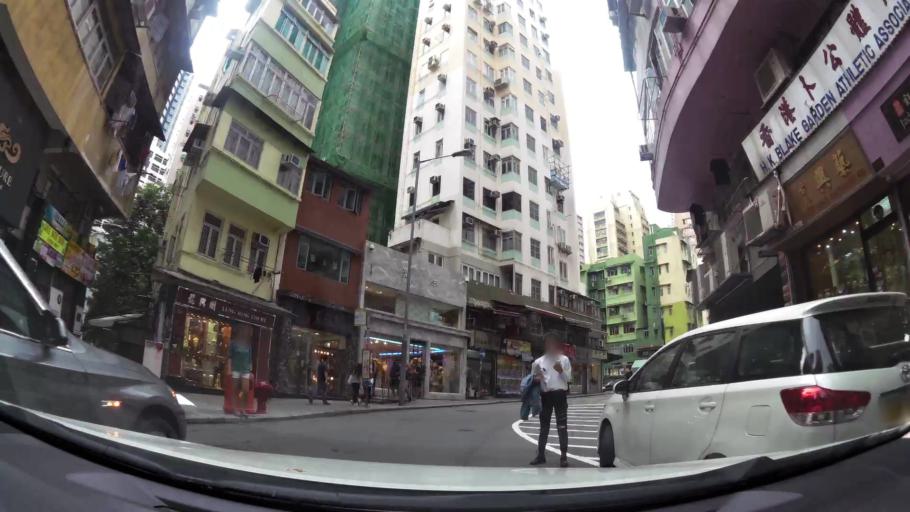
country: HK
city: Hong Kong
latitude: 22.2857
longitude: 114.1480
